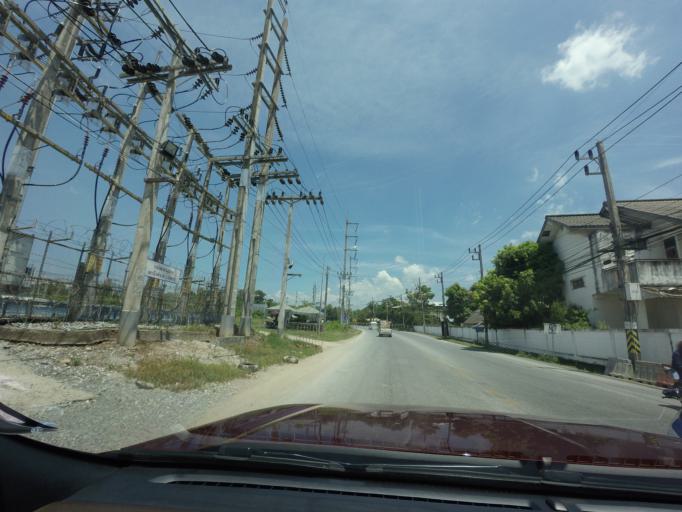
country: TH
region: Yala
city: Yala
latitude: 6.5541
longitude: 101.2711
